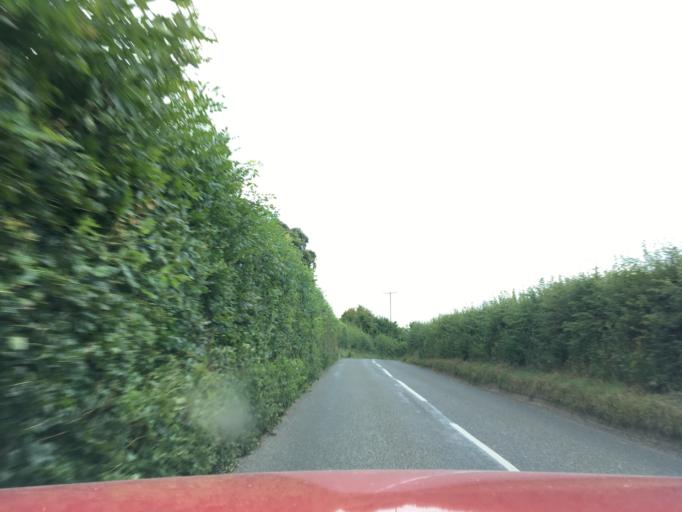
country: GB
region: England
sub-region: Oxfordshire
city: Faringdon
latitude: 51.6284
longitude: -1.5836
